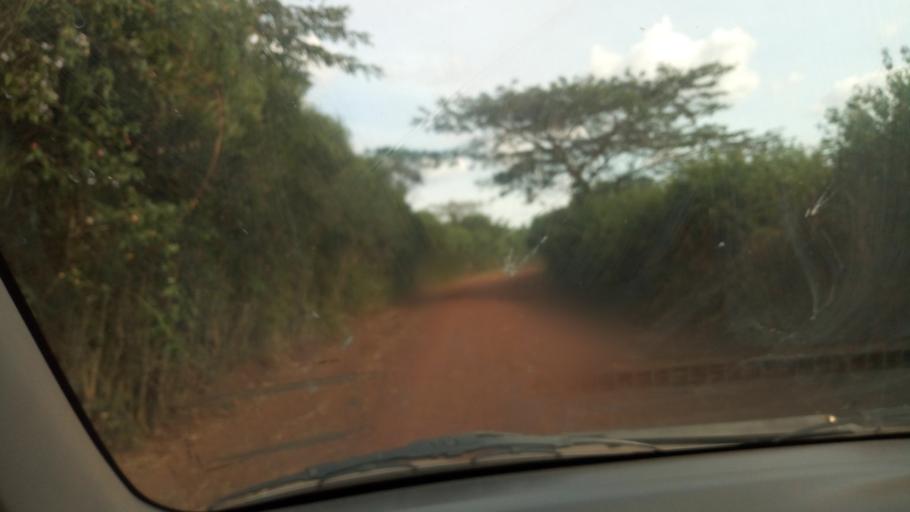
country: UG
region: Western Region
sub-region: Kiryandongo District
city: Kiryandongo
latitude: 1.8161
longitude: 31.9354
